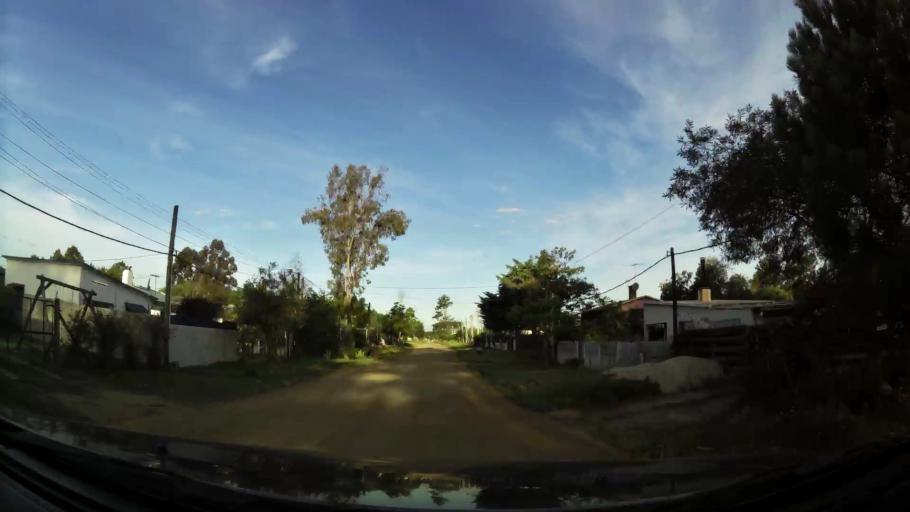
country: UY
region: Canelones
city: Atlantida
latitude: -34.7648
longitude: -55.8422
